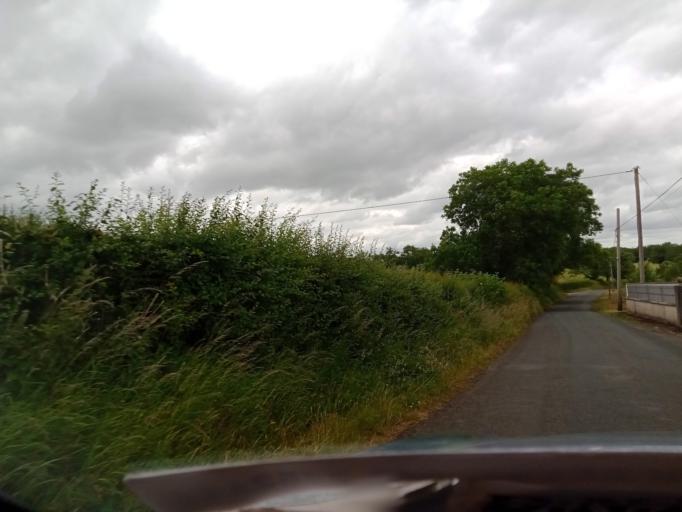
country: IE
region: Leinster
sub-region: Kilkenny
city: Thomastown
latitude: 52.5676
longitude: -7.1974
